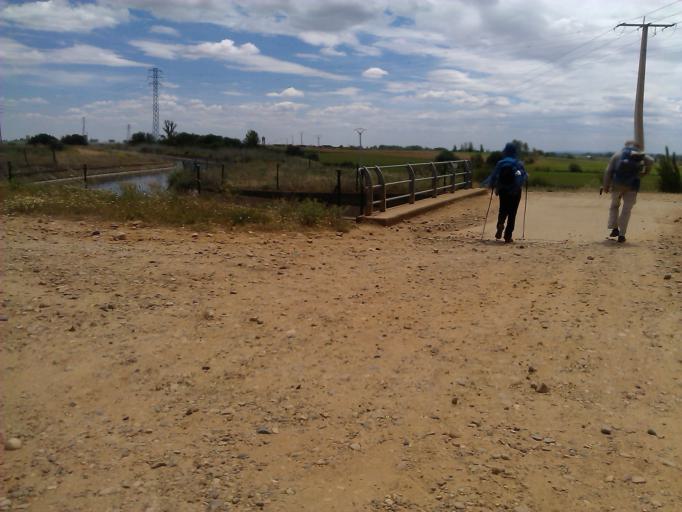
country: ES
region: Castille and Leon
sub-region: Provincia de Leon
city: Bustillo del Paramo
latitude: 42.4600
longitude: -5.7973
